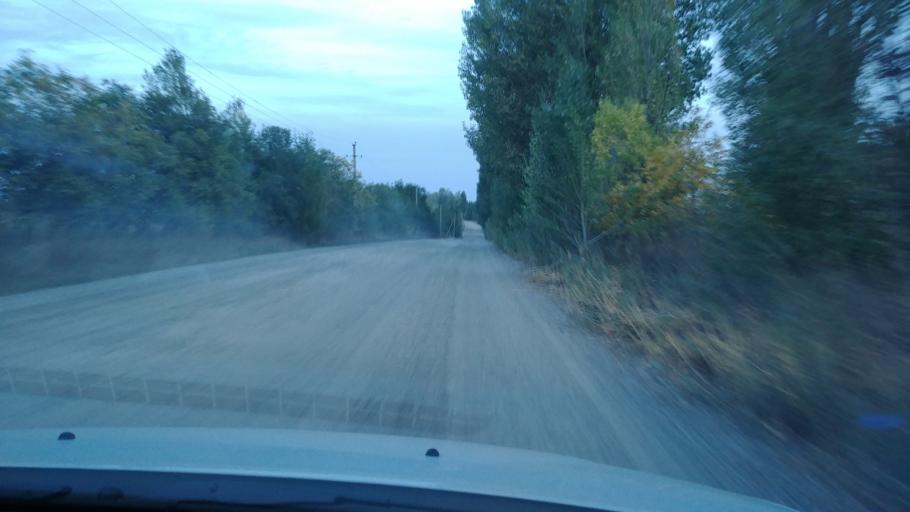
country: MD
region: Rezina
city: Saharna
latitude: 47.6786
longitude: 28.9216
